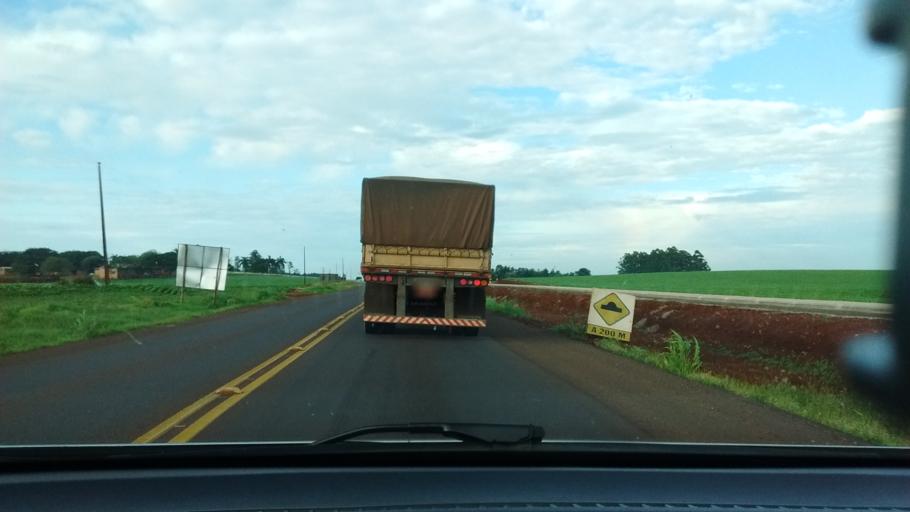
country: BR
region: Parana
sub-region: Cascavel
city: Cascavel
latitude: -25.0784
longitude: -53.5791
